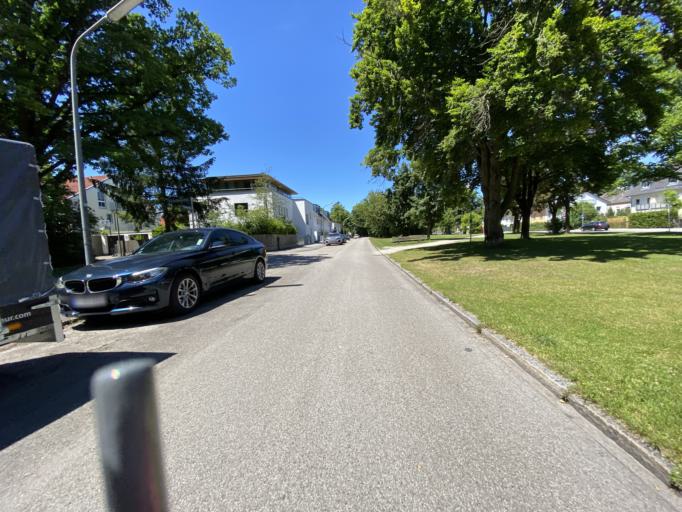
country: DE
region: Bavaria
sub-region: Upper Bavaria
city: Neubiberg
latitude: 48.1191
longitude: 11.6514
